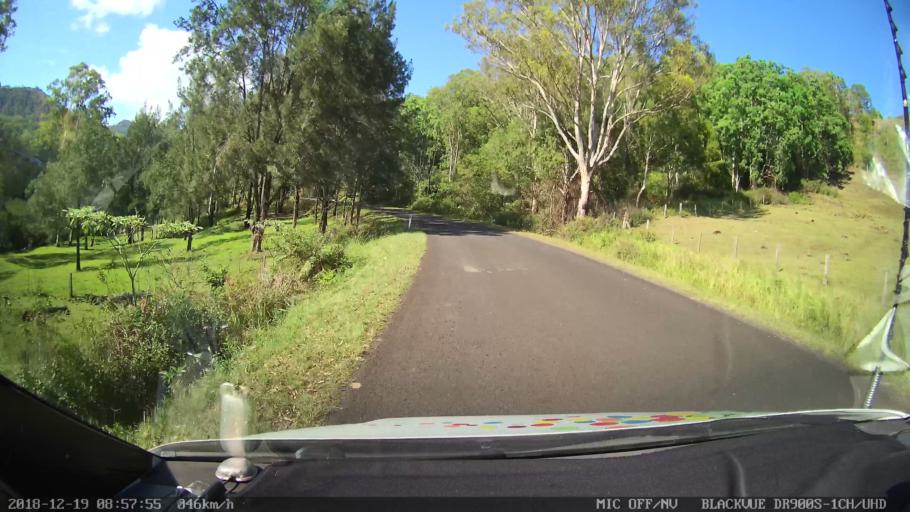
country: AU
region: New South Wales
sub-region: Kyogle
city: Kyogle
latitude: -28.4218
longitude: 152.9682
